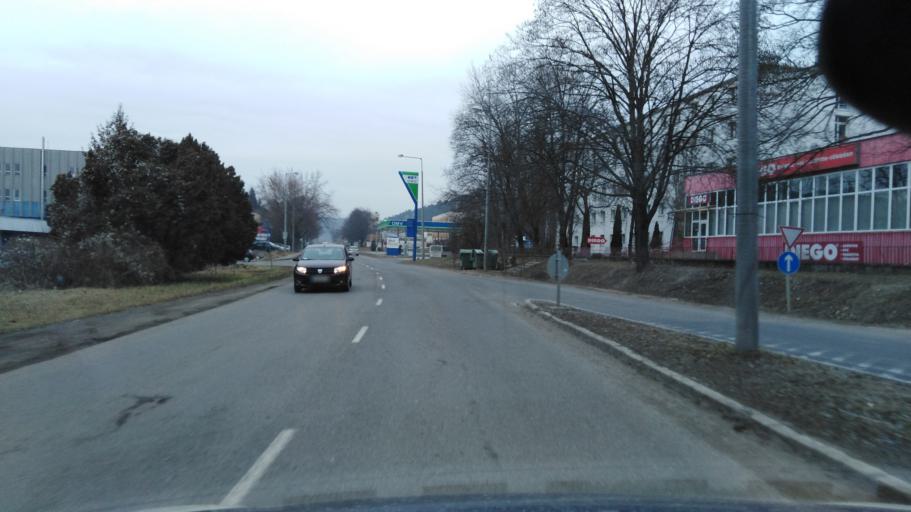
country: HU
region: Nograd
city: Salgotarjan
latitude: 48.0800
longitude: 19.7933
